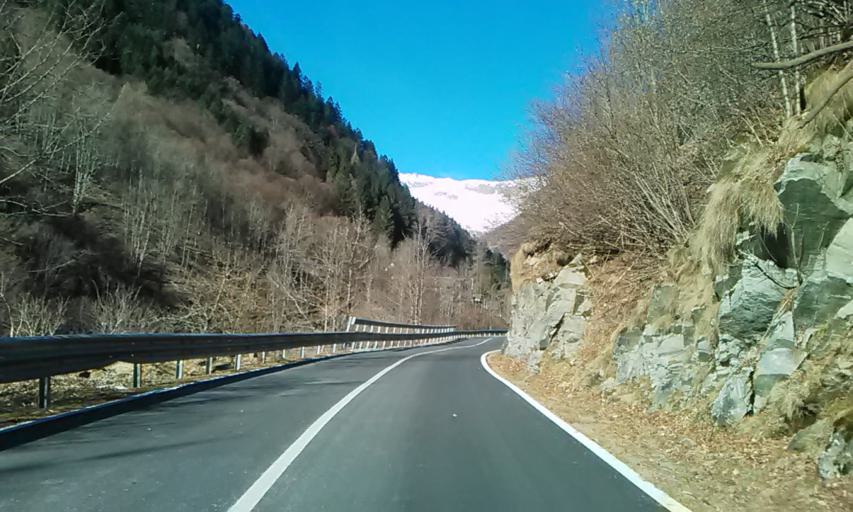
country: IT
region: Piedmont
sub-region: Provincia di Vercelli
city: Carcoforo
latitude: 45.8940
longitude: 8.0617
